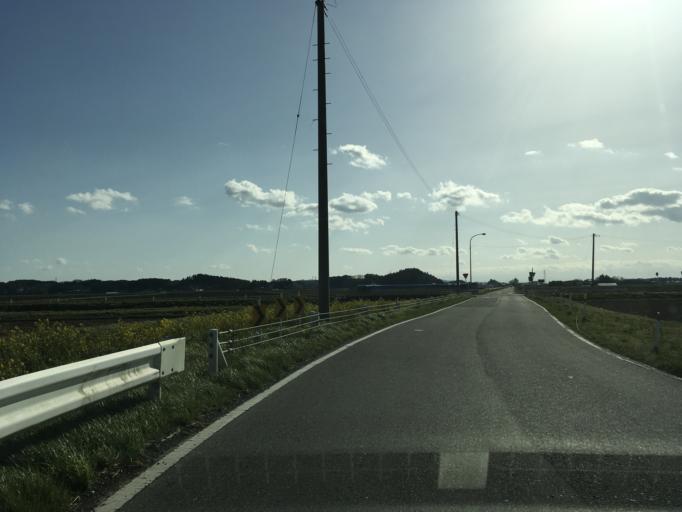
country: JP
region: Miyagi
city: Wakuya
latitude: 38.6555
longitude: 141.2378
